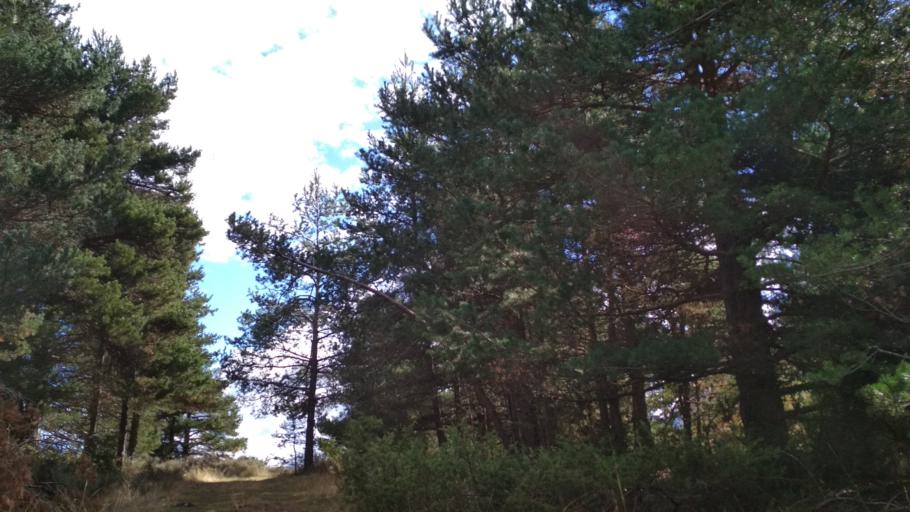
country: ES
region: Catalonia
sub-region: Provincia de Lleida
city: Toloriu
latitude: 42.3320
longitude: 1.6588
